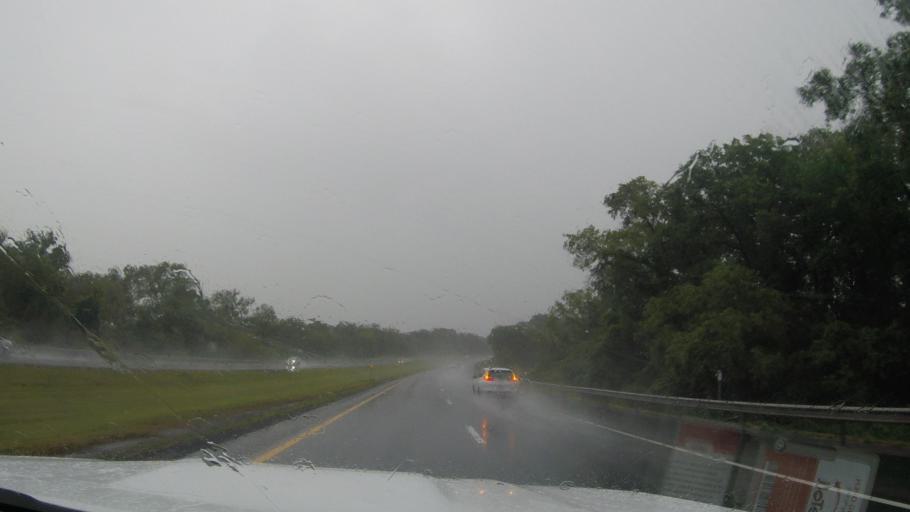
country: US
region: New York
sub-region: Ontario County
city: Geneva
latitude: 42.9594
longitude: -76.9497
